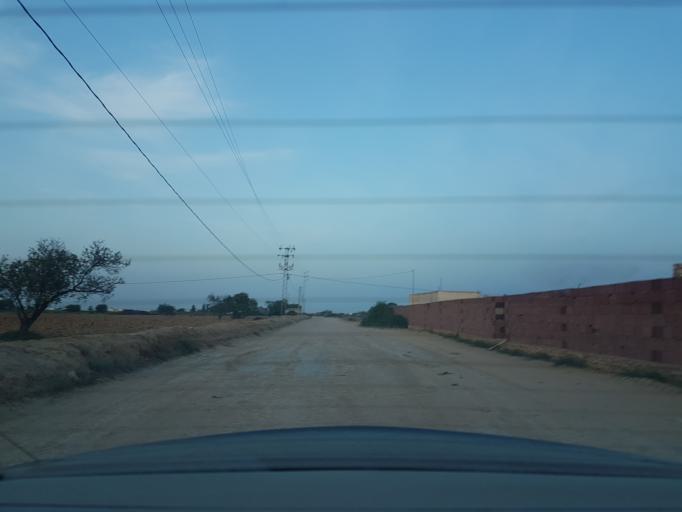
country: TN
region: Safaqis
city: Sfax
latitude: 34.7033
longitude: 10.6801
